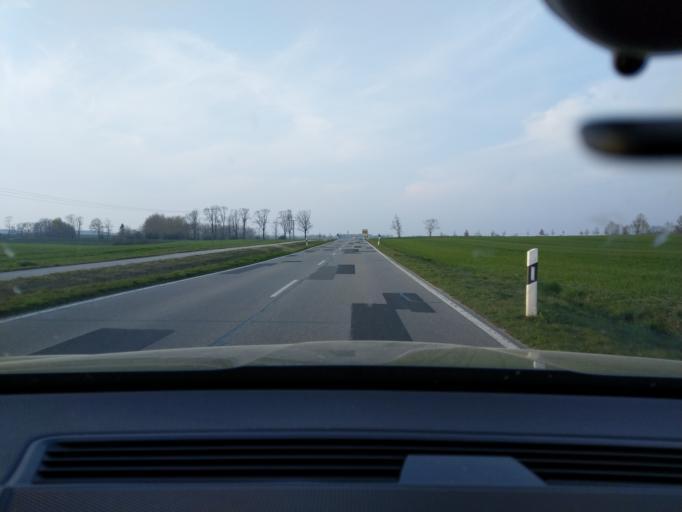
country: DE
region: Mecklenburg-Vorpommern
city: Prohn
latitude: 54.3460
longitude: 13.0297
